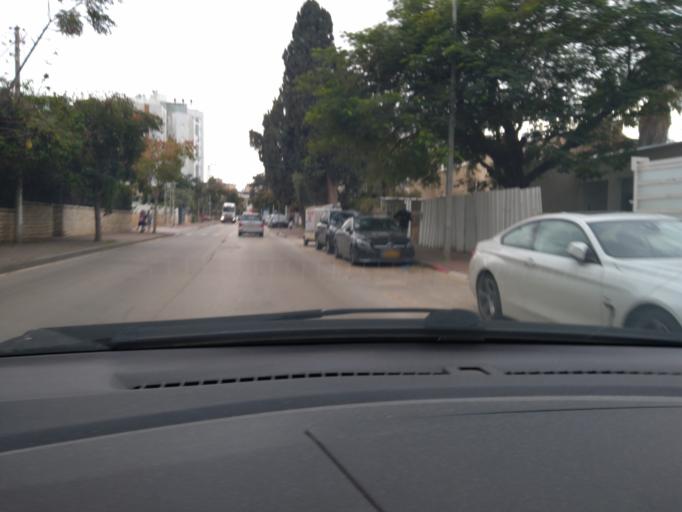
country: IL
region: Central District
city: Netanya
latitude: 32.3438
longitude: 34.8622
